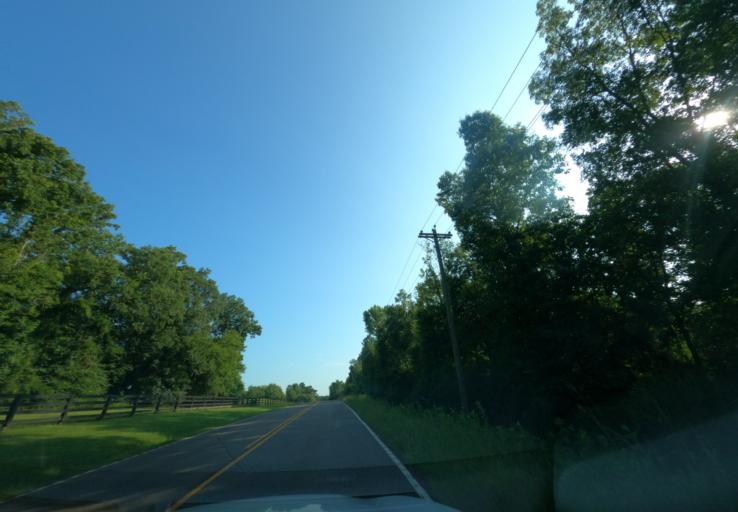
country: US
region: South Carolina
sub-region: Edgefield County
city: Murphys Estates
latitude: 33.6507
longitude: -81.9741
